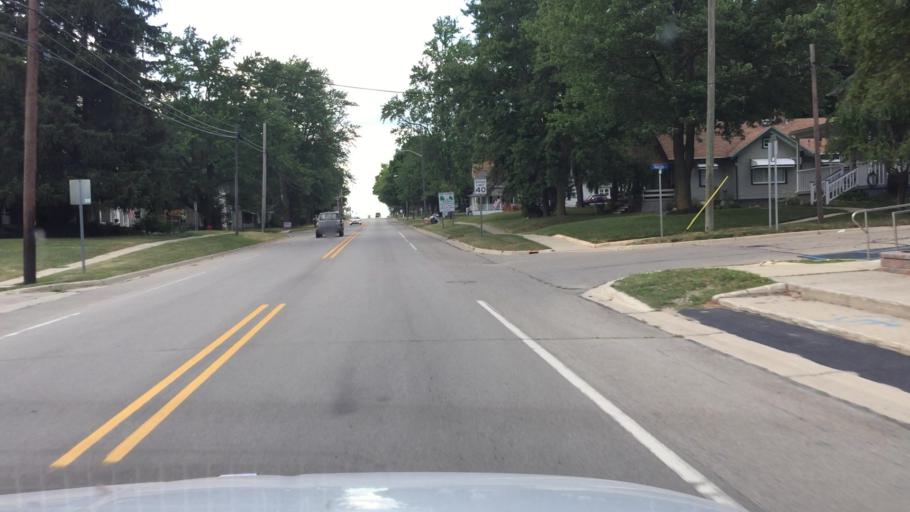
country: US
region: Michigan
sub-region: Saint Clair County
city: Yale
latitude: 43.1343
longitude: -82.7986
